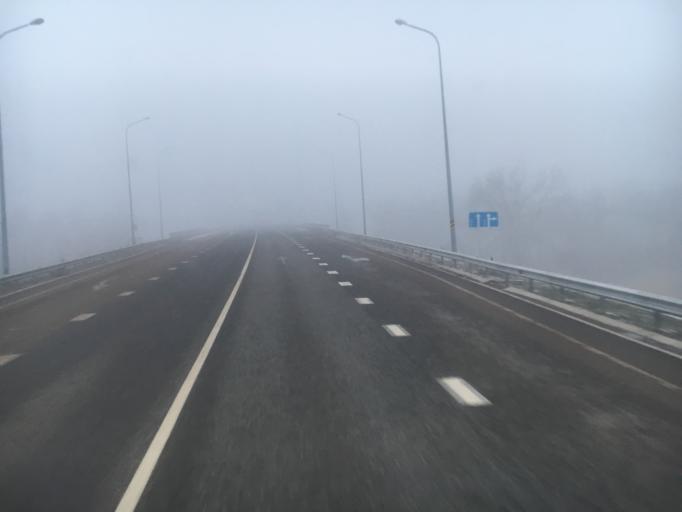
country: KZ
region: Zhambyl
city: Taraz
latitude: 42.9981
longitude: 71.2413
